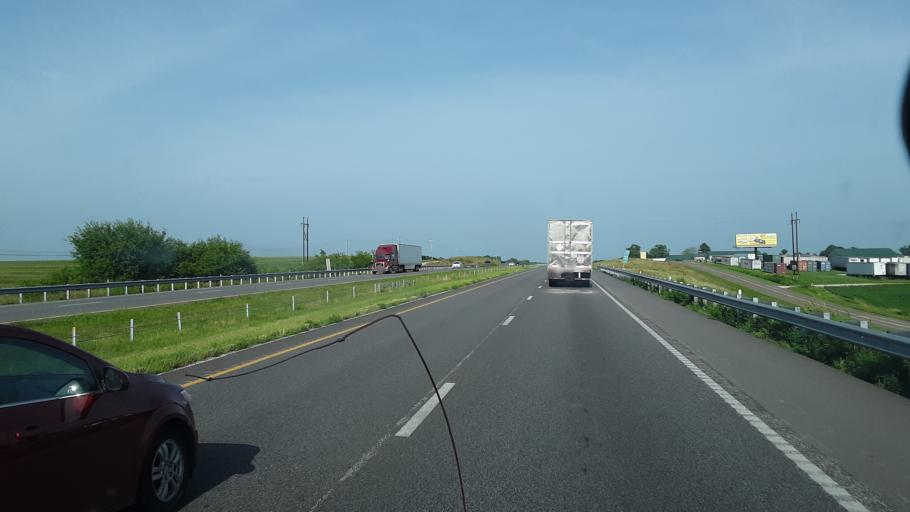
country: US
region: Missouri
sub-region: Lafayette County
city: Odessa
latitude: 39.0059
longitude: -93.9000
